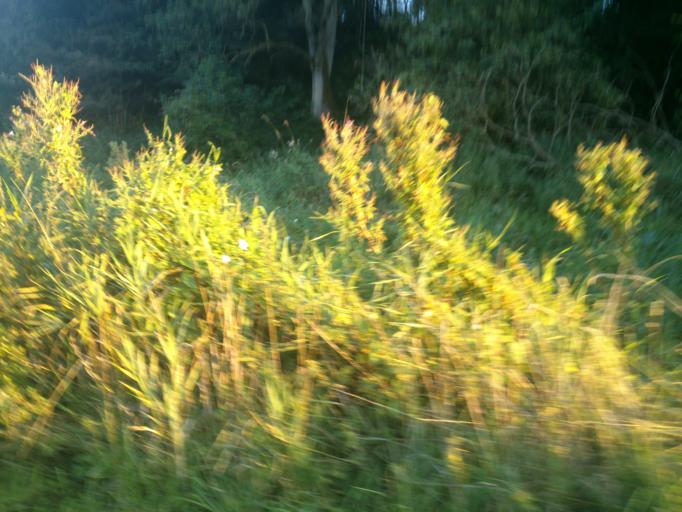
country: DK
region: South Denmark
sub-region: Fredericia Kommune
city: Fredericia
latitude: 55.5726
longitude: 9.7051
